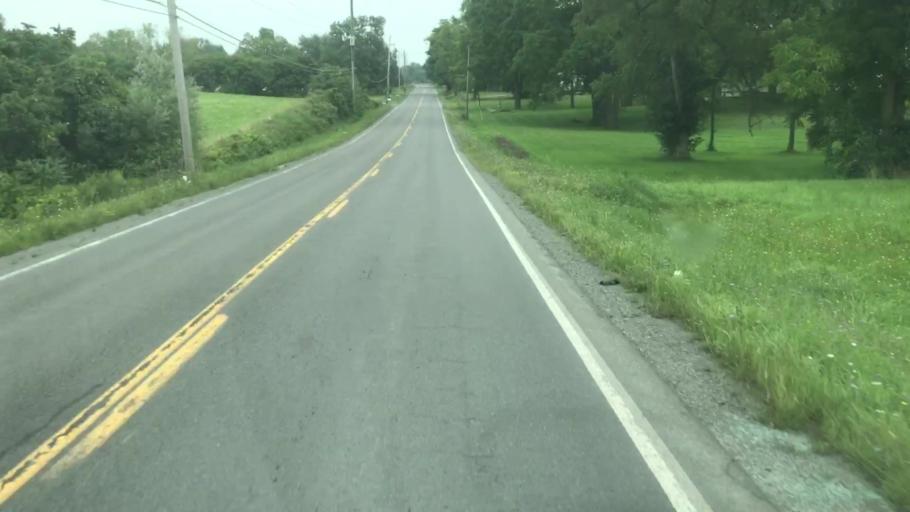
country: US
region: New York
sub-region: Cayuga County
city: Melrose Park
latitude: 42.9542
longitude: -76.5009
